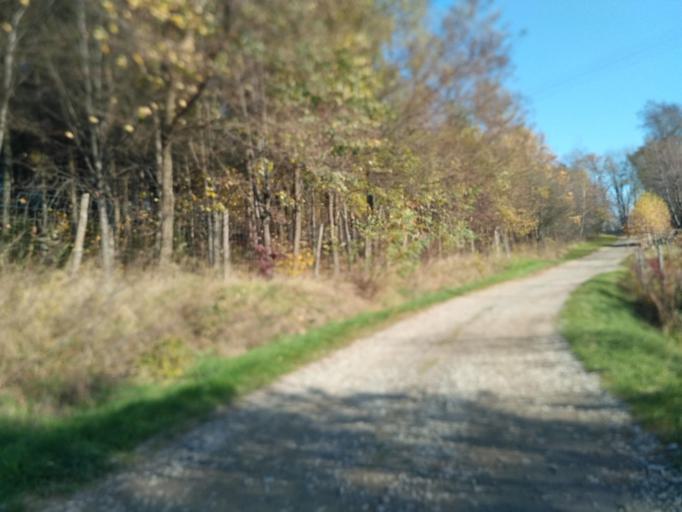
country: PL
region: Subcarpathian Voivodeship
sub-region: Powiat rzeszowski
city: Blazowa
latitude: 49.8573
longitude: 22.0806
